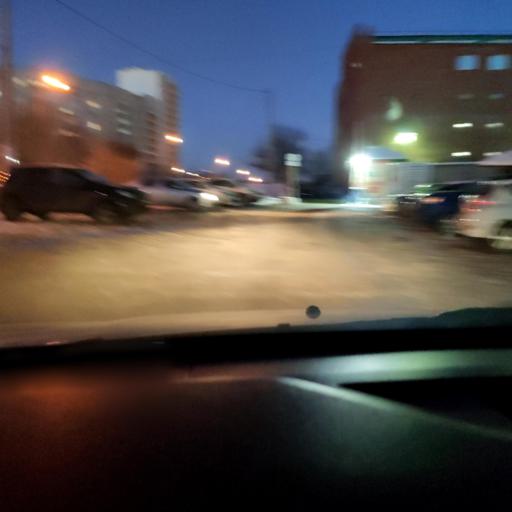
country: RU
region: Samara
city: Samara
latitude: 53.2134
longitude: 50.2143
